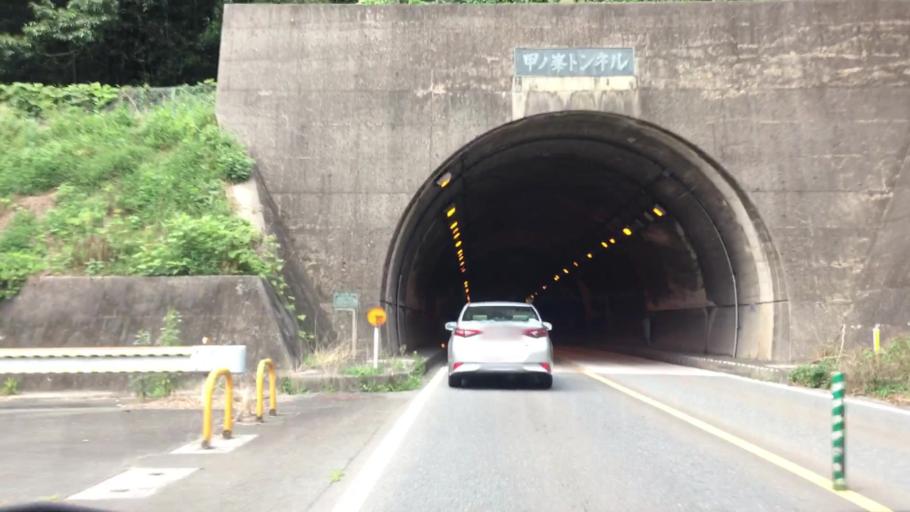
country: JP
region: Saga Prefecture
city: Karatsu
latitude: 33.4766
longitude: 130.0462
